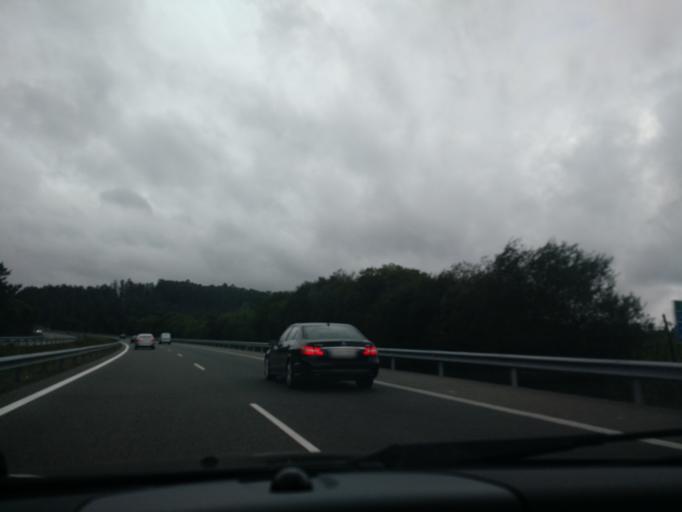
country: ES
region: Galicia
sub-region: Provincia da Coruna
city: Abegondo
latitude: 43.2251
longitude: -8.2736
